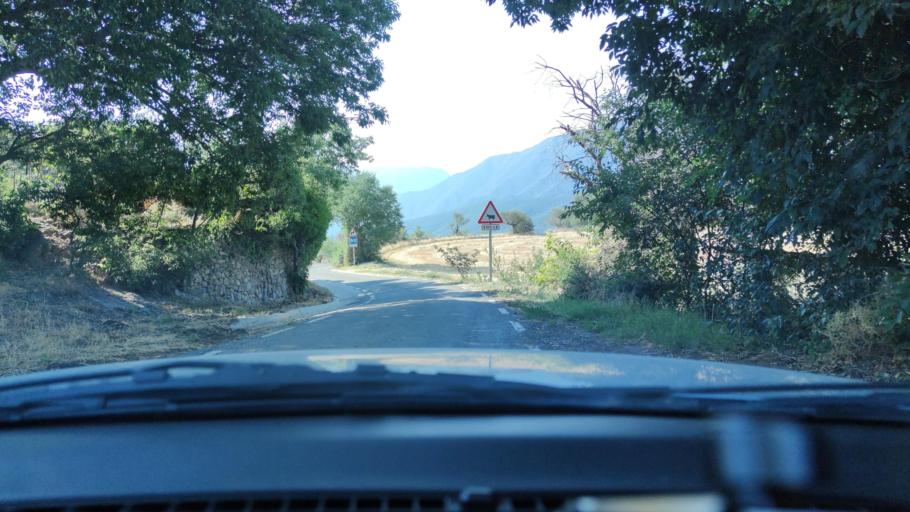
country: ES
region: Catalonia
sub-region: Provincia de Lleida
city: Llimiana
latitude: 42.0854
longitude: 0.8410
